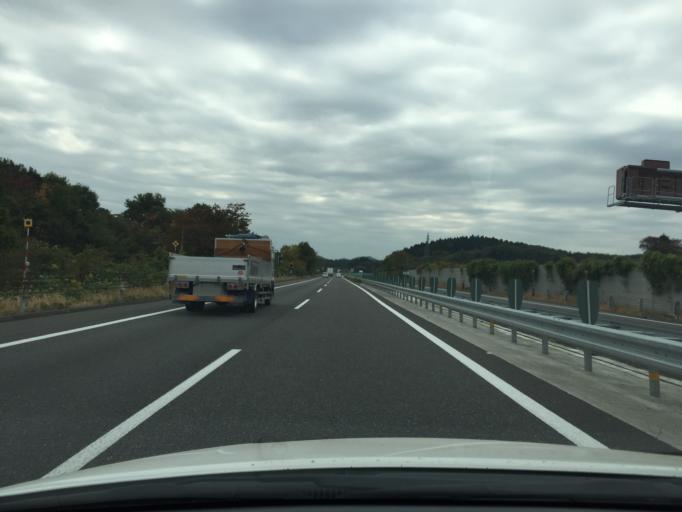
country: JP
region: Fukushima
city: Sukagawa
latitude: 37.1921
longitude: 140.2948
